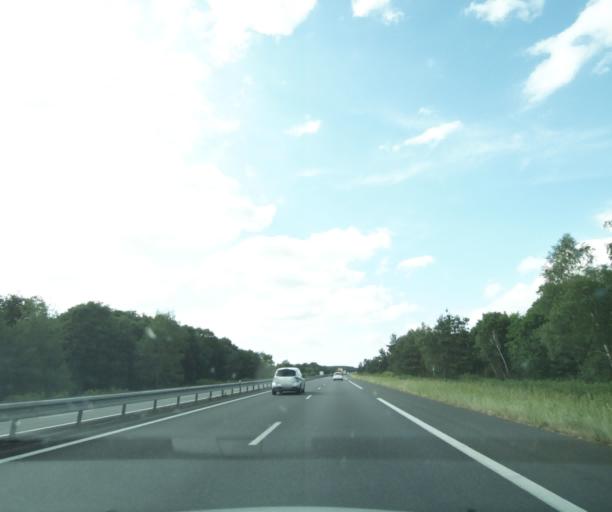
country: FR
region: Centre
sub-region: Departement du Loiret
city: Jouy-le-Potier
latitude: 47.7423
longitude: 1.8671
